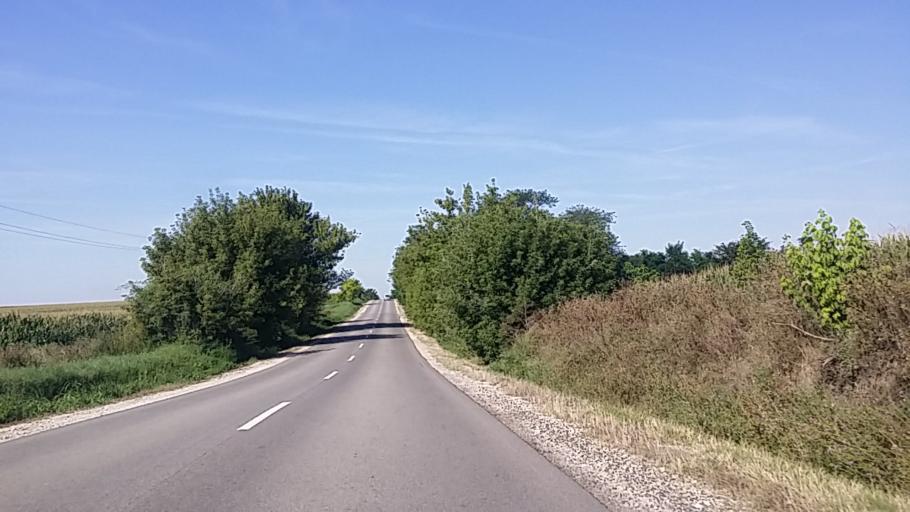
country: HU
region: Fejer
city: Pusztaszabolcs
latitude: 47.1088
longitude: 18.7459
